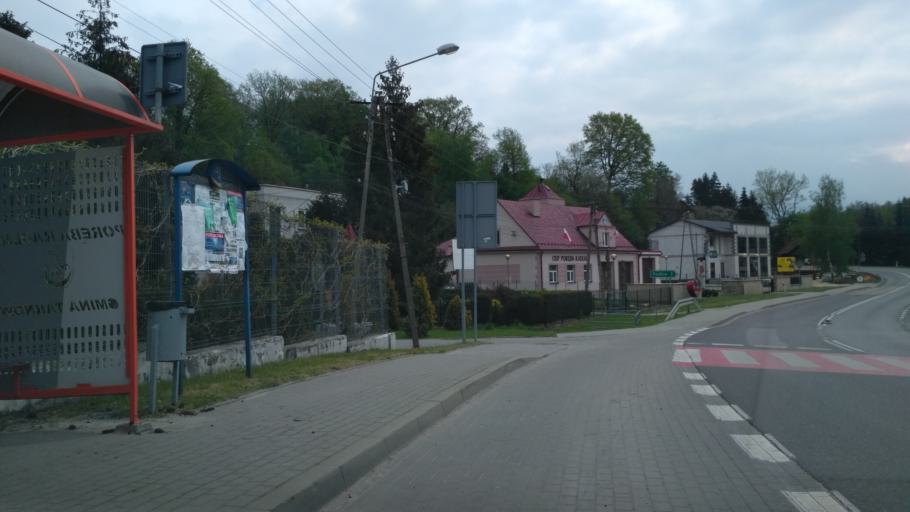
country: PL
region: Lesser Poland Voivodeship
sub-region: Powiat tarnowski
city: Tarnowiec
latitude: 49.9590
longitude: 20.9932
